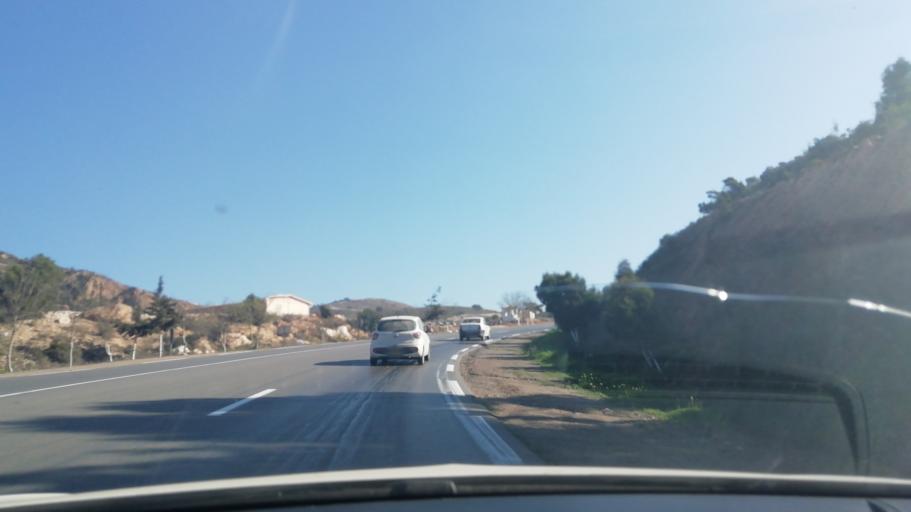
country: DZ
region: Tlemcen
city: Nedroma
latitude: 35.0903
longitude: -1.8206
